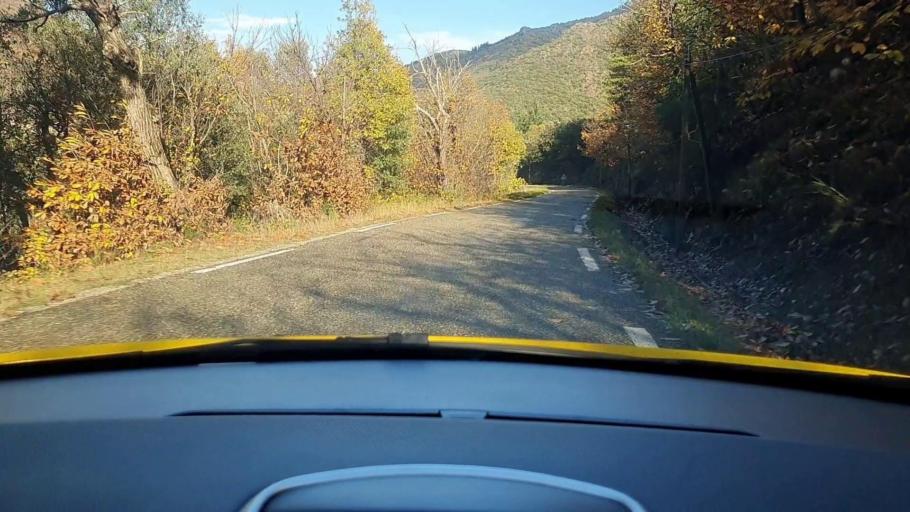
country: FR
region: Languedoc-Roussillon
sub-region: Departement du Gard
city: Valleraugue
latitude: 44.1629
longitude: 3.6558
